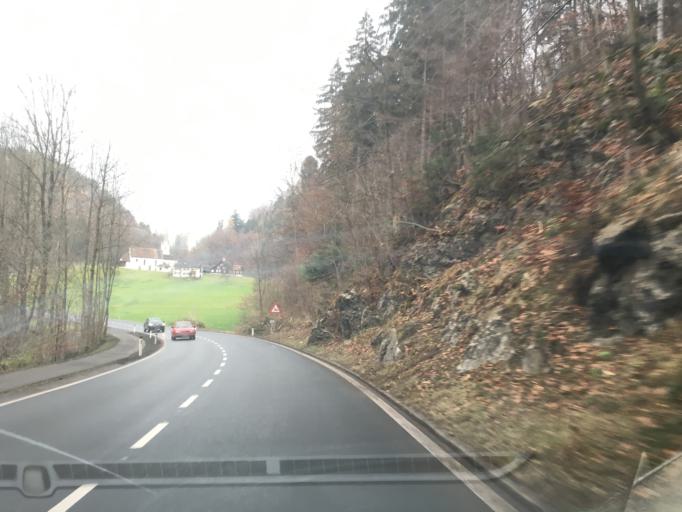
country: AT
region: Vorarlberg
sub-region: Politischer Bezirk Feldkirch
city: Klaus
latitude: 47.3217
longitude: 9.6439
